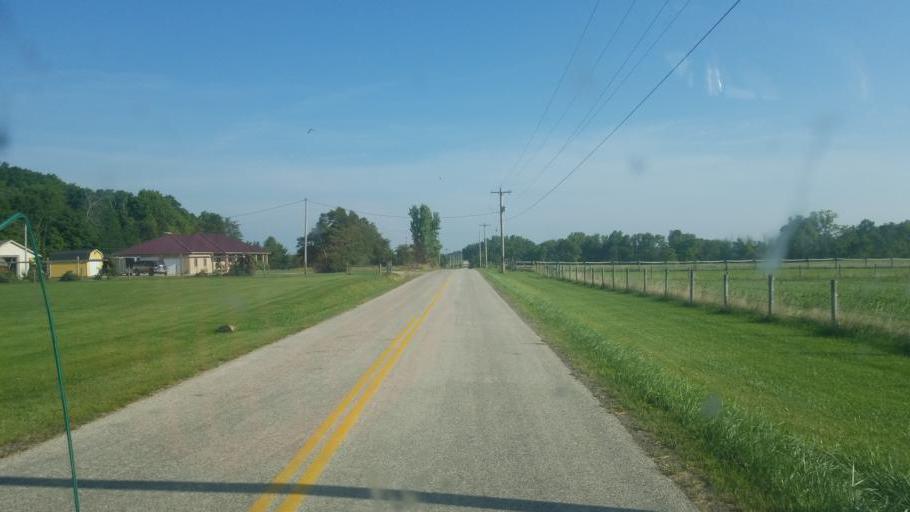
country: US
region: Ohio
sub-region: Huron County
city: New London
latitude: 41.0201
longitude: -82.3539
